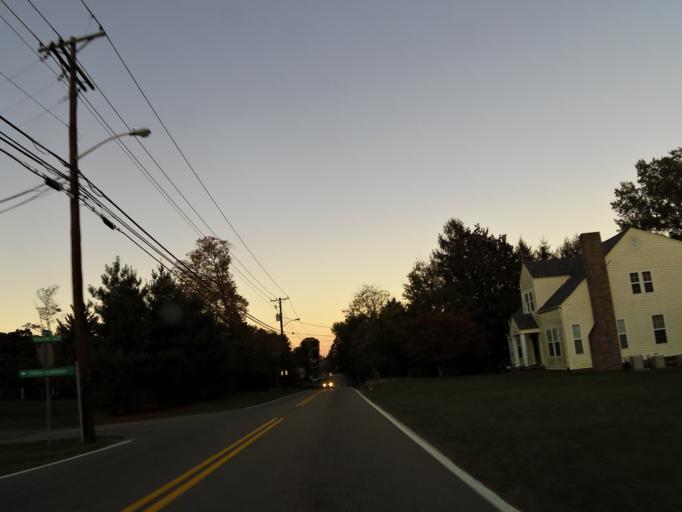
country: US
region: Tennessee
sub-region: Knox County
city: Knoxville
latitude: 36.0225
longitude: -83.9585
